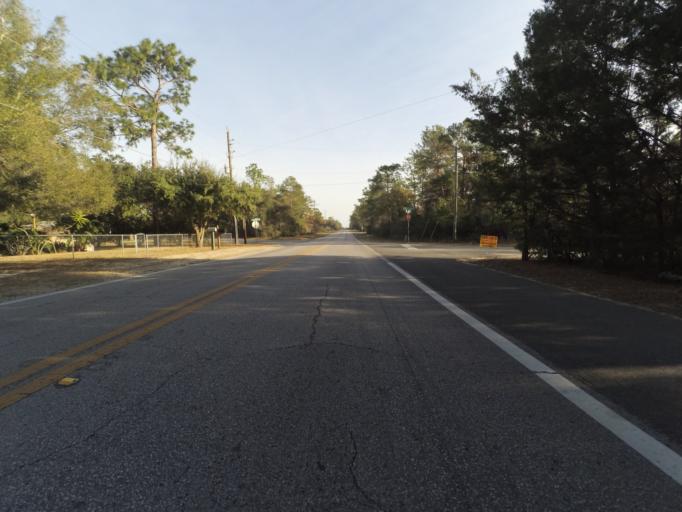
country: US
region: Florida
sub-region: Lake County
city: Umatilla
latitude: 28.9376
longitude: -81.6400
